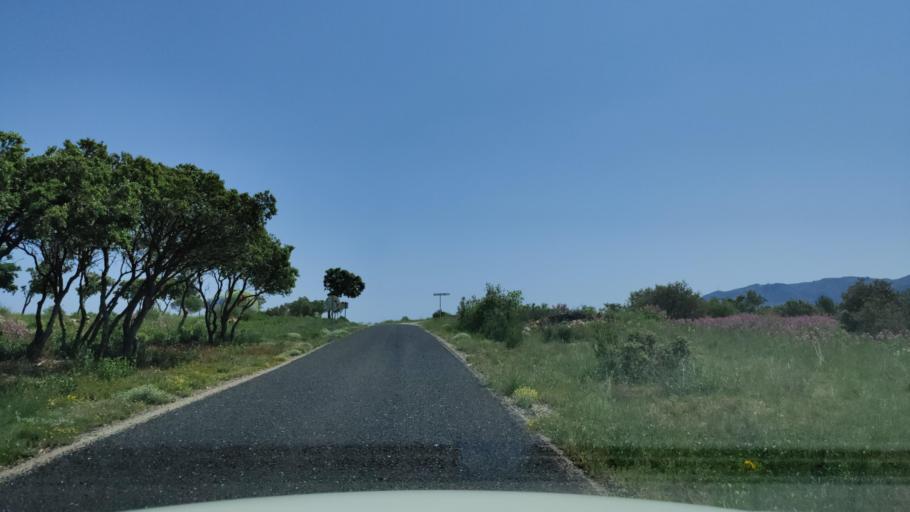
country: FR
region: Languedoc-Roussillon
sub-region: Departement des Pyrenees-Orientales
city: Estagel
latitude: 42.7890
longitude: 2.7391
